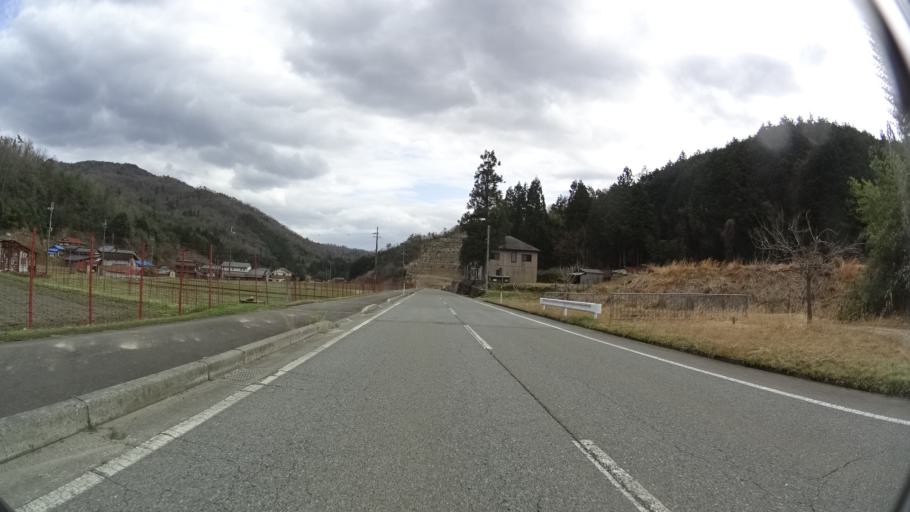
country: JP
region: Hyogo
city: Toyooka
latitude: 35.4858
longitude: 134.9232
